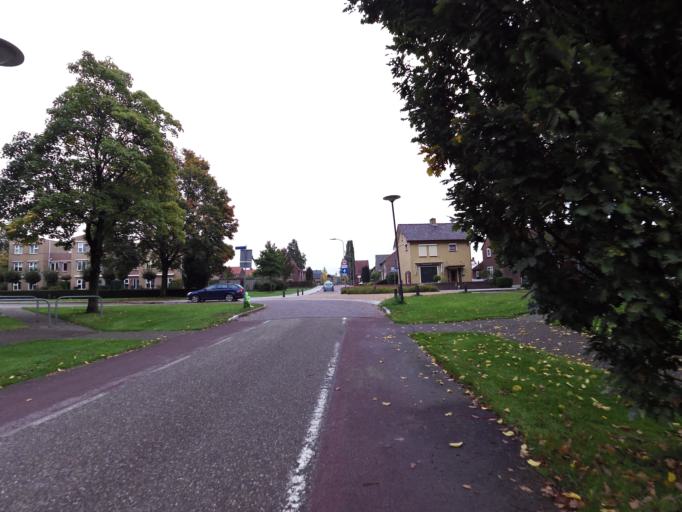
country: NL
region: Gelderland
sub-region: Oude IJsselstreek
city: Gendringen
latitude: 51.8883
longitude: 6.3799
